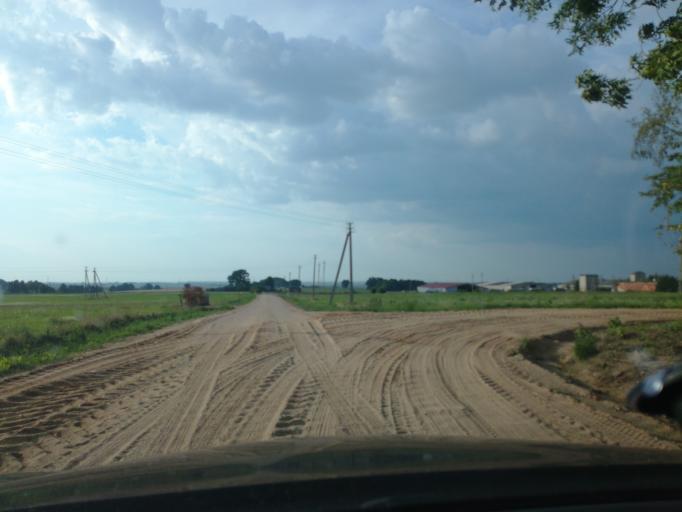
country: LT
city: Simnas
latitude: 54.3901
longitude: 23.8174
